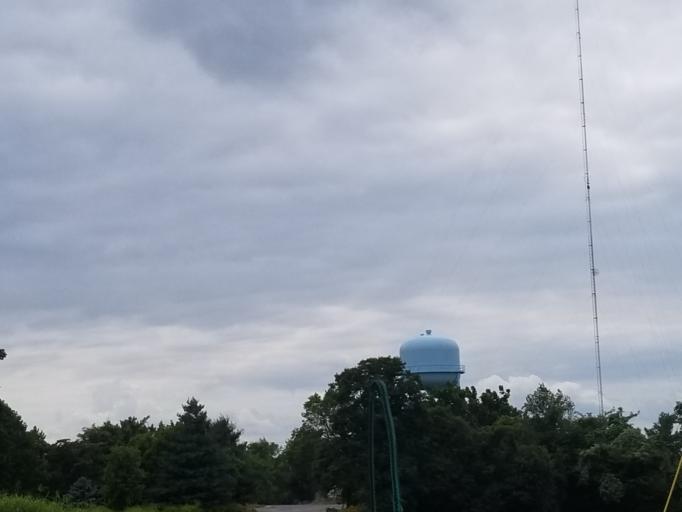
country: US
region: Illinois
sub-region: Jackson County
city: Murphysboro
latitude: 37.7002
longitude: -89.3677
